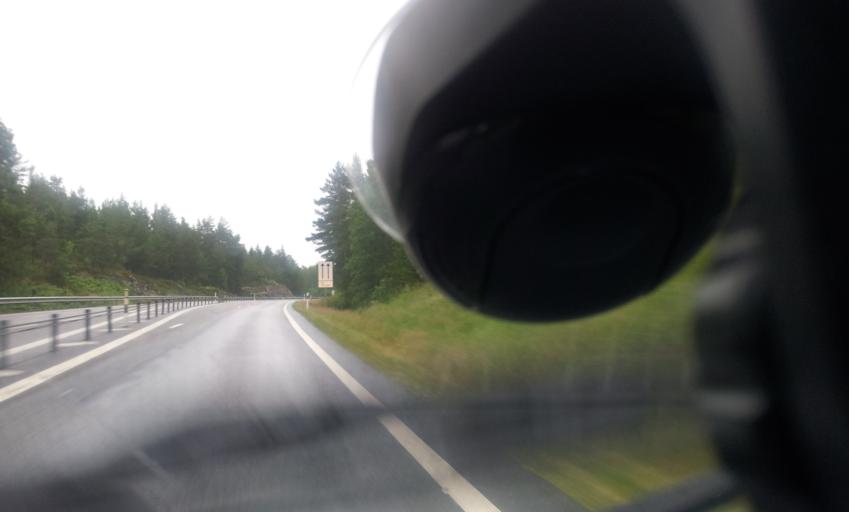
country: SE
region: OEstergoetland
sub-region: Valdemarsviks Kommun
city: Valdemarsvik
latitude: 58.0928
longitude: 16.5252
